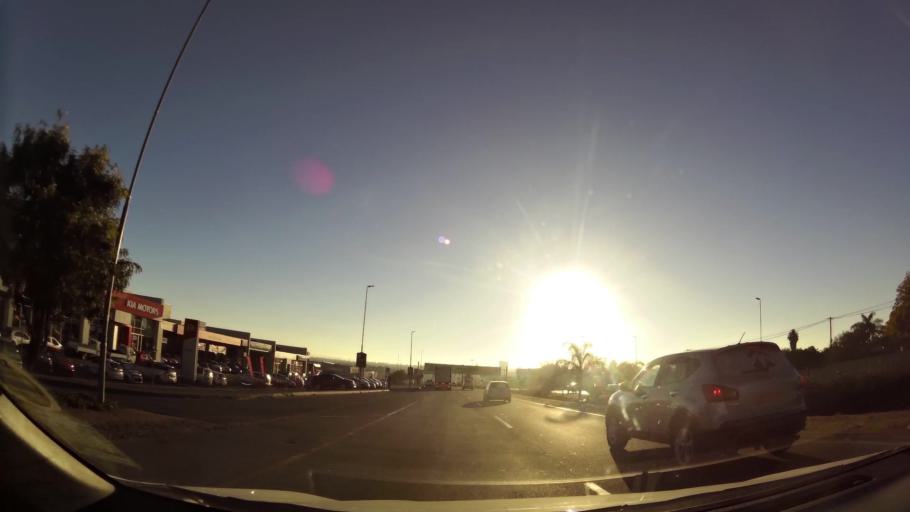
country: ZA
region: Limpopo
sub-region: Capricorn District Municipality
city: Polokwane
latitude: -23.9178
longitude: 29.4413
